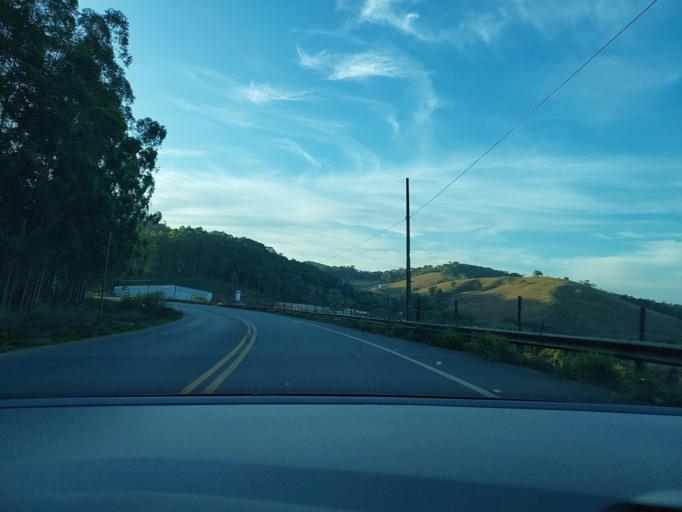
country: BR
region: Minas Gerais
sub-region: Vicosa
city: Vicosa
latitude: -20.8227
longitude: -42.8195
